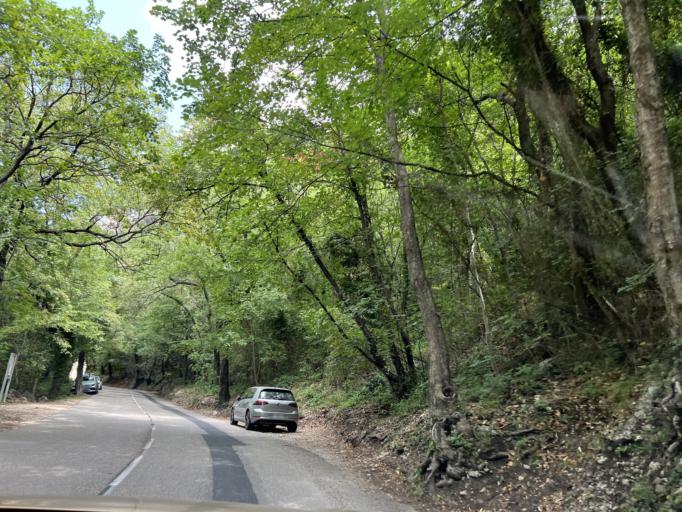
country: FR
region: Provence-Alpes-Cote d'Azur
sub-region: Departement des Alpes-Maritimes
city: Le Rouret
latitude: 43.7257
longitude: 6.9967
